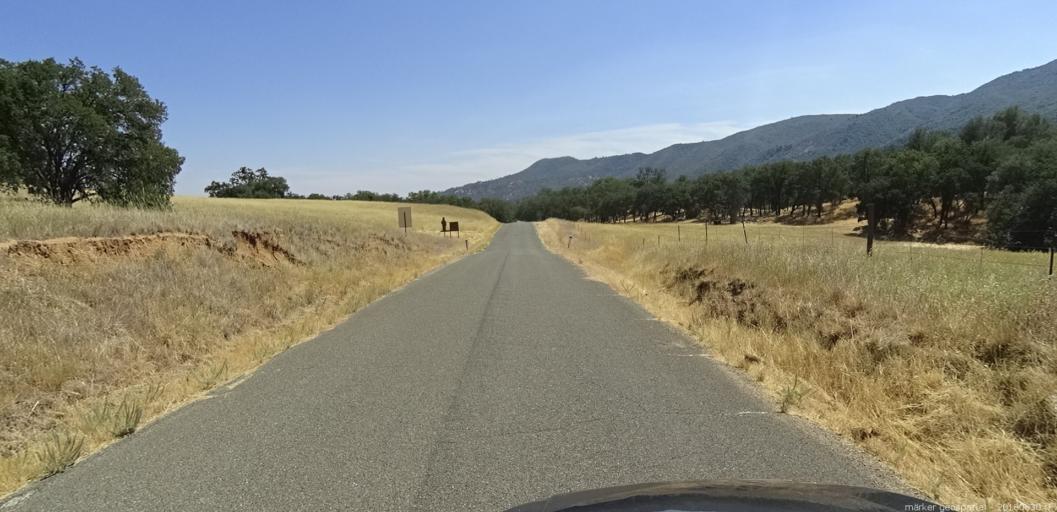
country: US
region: California
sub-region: Monterey County
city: King City
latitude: 35.9844
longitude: -121.3507
